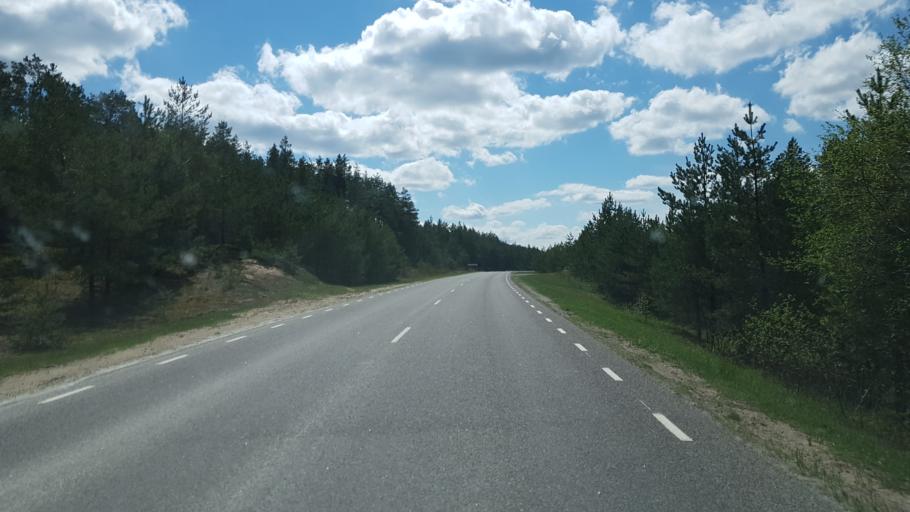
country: EE
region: Harju
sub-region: Kuusalu vald
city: Kuusalu
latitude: 59.4306
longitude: 25.3863
